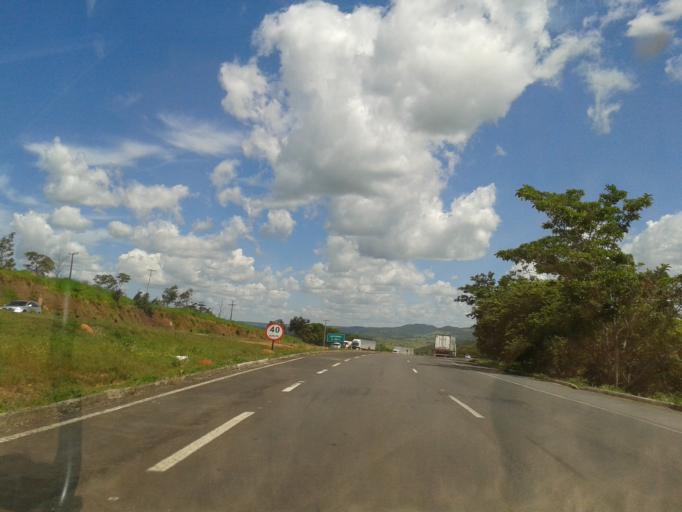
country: BR
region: Goias
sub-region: Piracanjuba
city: Piracanjuba
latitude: -17.3733
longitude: -49.2407
